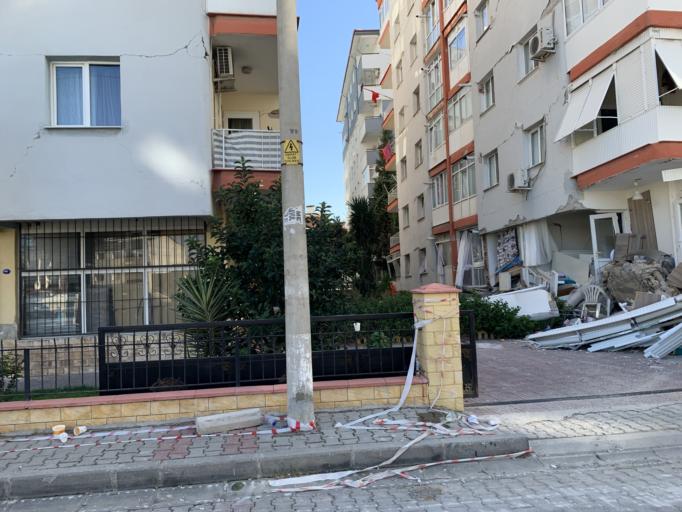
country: TR
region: Izmir
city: Bornova
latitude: 38.4616
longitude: 27.1803
